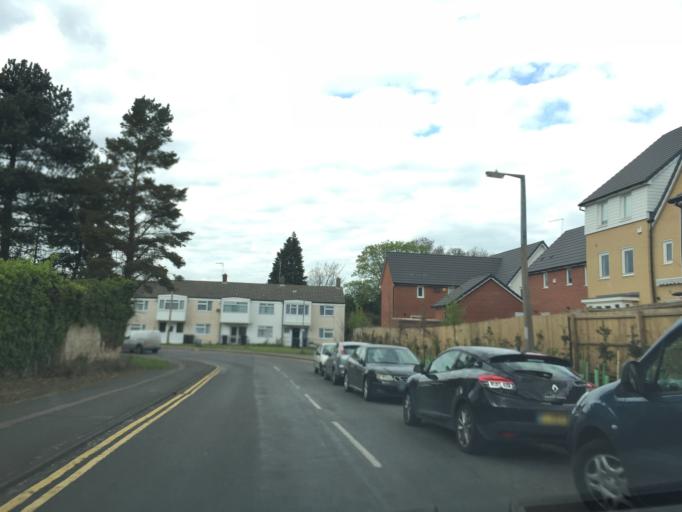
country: GB
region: England
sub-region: Essex
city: Harlow
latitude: 51.7756
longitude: 0.0910
